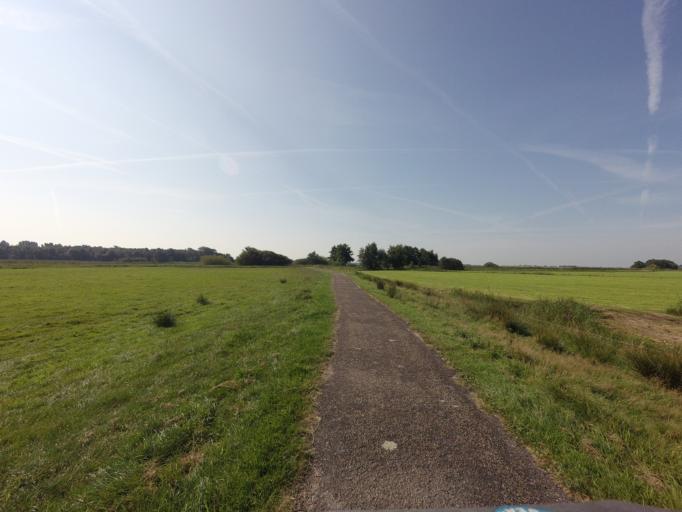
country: NL
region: Overijssel
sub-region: Gemeente Steenwijkerland
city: Oldemarkt
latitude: 52.8449
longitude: 5.9742
